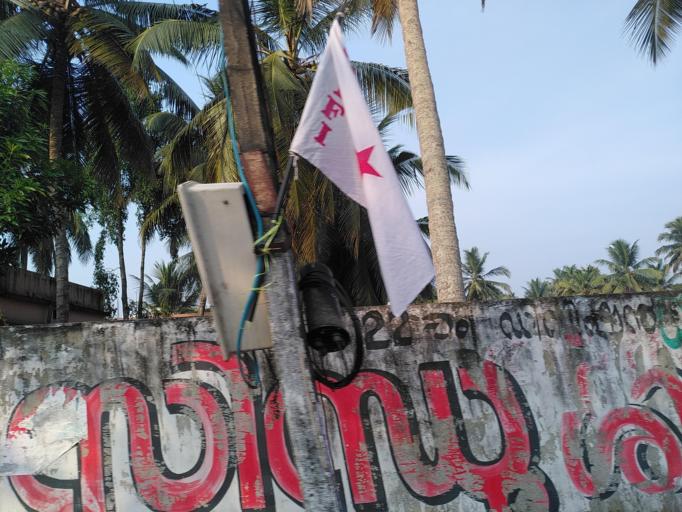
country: IN
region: Kerala
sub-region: Alappuzha
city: Arukutti
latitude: 9.9292
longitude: 76.3271
